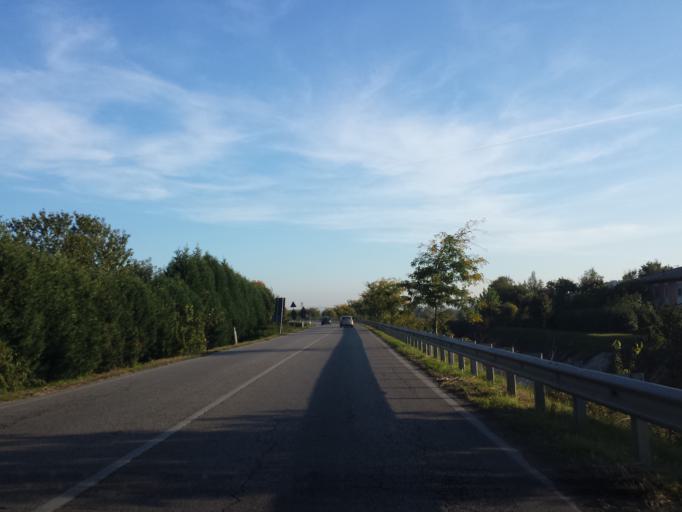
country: IT
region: Veneto
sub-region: Provincia di Vicenza
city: Castelnovo
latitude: 45.6138
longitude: 11.4674
